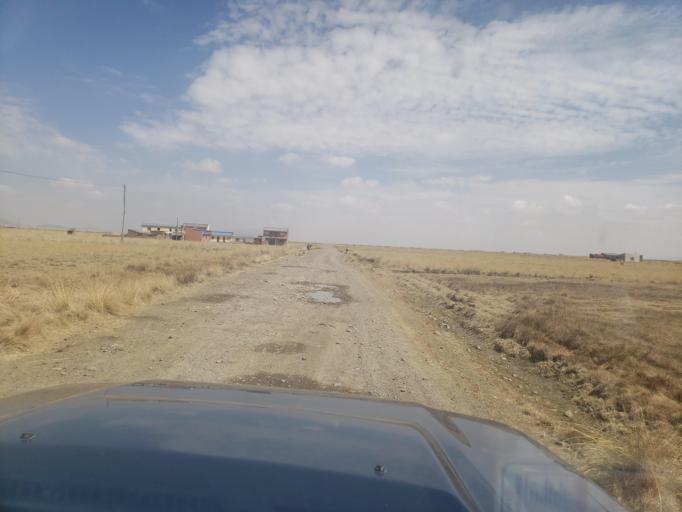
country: BO
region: La Paz
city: Batallas
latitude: -16.4264
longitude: -68.3990
